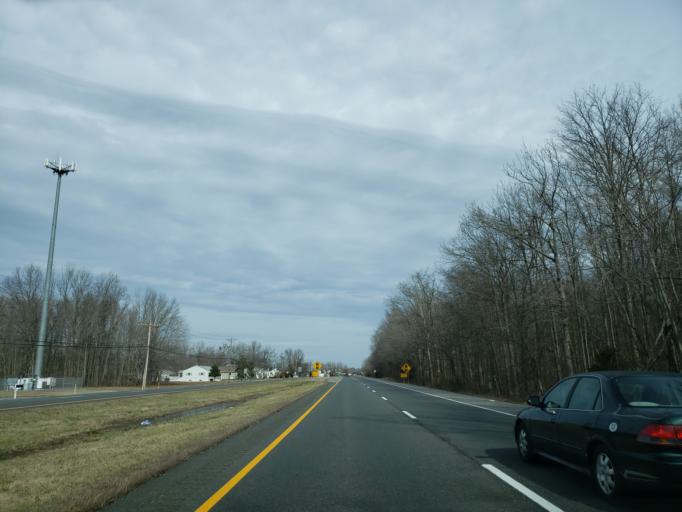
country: US
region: Delaware
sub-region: New Castle County
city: Townsend
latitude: 39.4023
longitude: -75.6617
